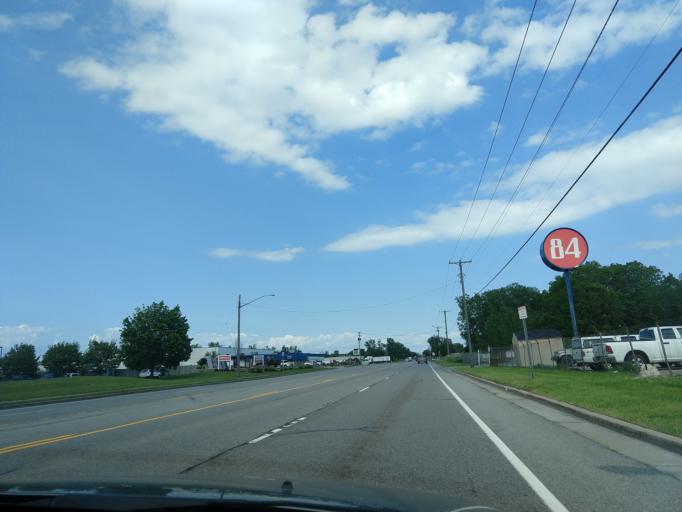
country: US
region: New York
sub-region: Erie County
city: Depew
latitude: 42.9128
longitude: -78.6904
